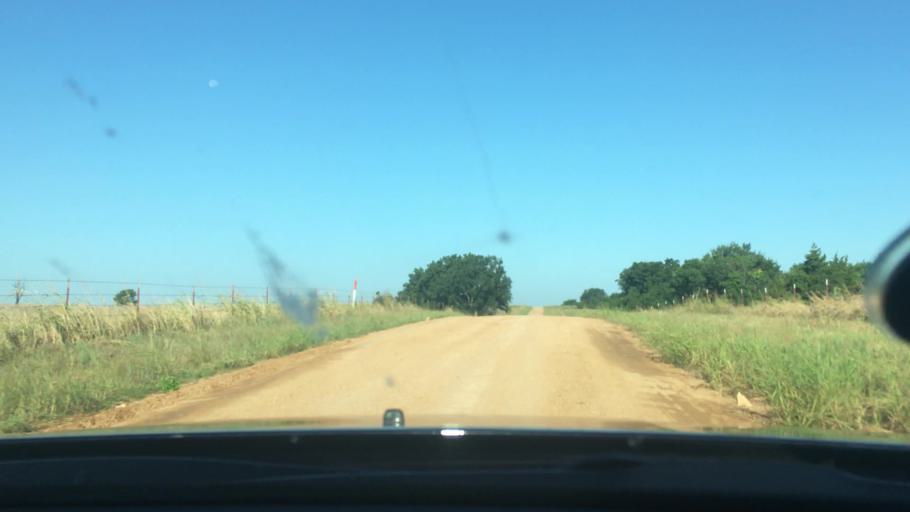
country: US
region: Oklahoma
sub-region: Murray County
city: Sulphur
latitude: 34.4194
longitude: -96.7837
